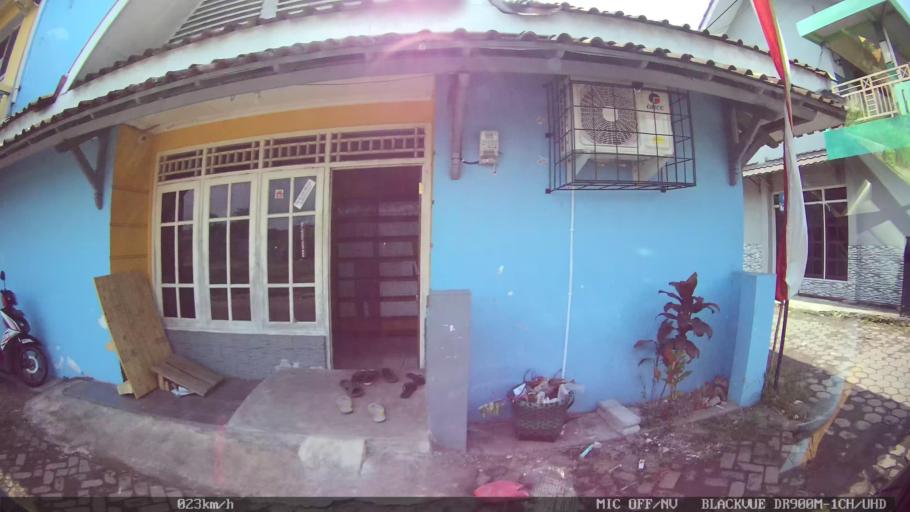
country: ID
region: Daerah Istimewa Yogyakarta
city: Yogyakarta
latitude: -7.8131
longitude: 110.4060
